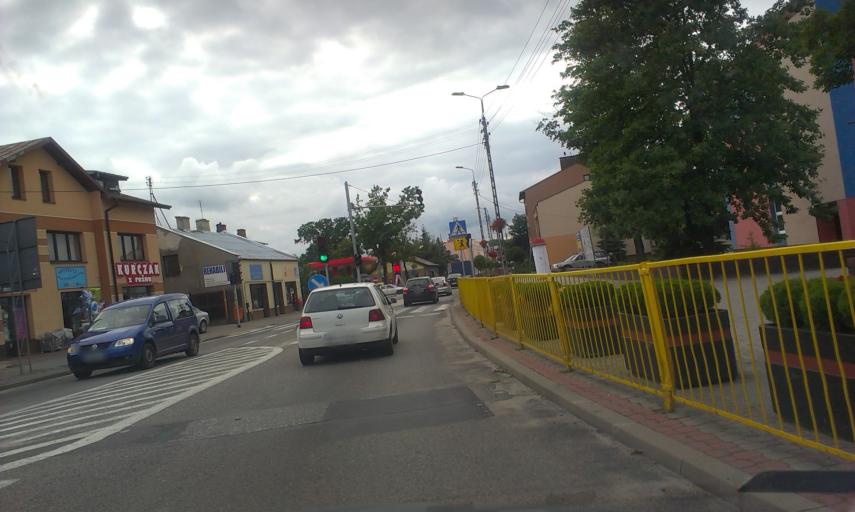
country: PL
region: Masovian Voivodeship
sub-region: Powiat zyrardowski
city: Mszczonow
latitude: 51.9742
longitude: 20.5183
